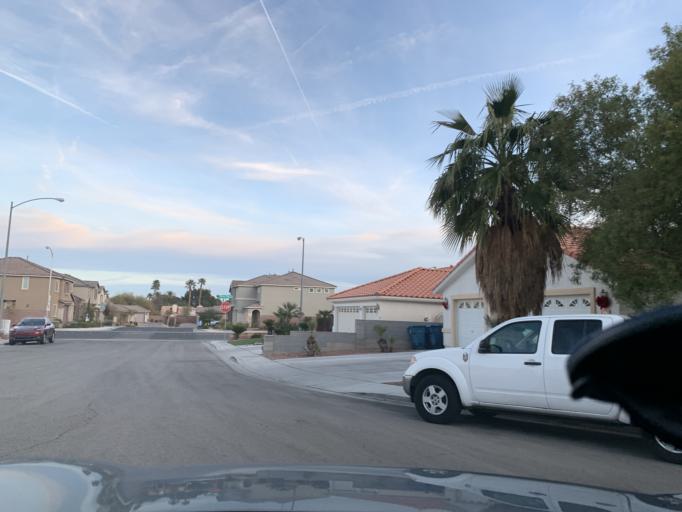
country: US
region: Nevada
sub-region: Clark County
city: Spring Valley
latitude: 36.0902
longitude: -115.2347
